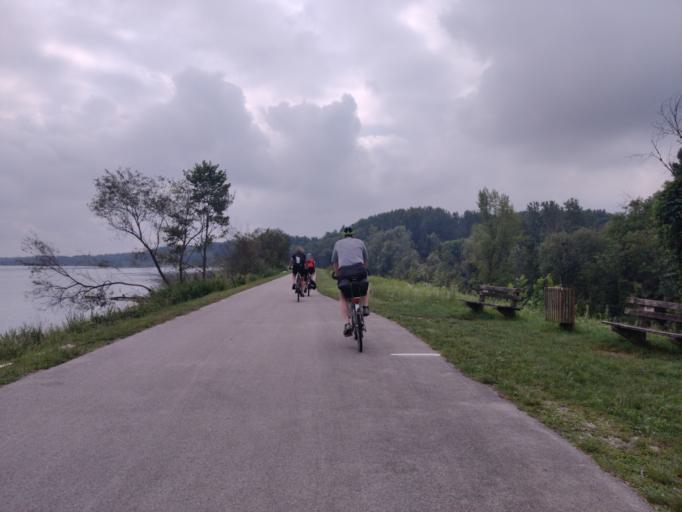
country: AT
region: Lower Austria
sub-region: Politischer Bezirk Sankt Polten
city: Traismauer
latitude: 48.3722
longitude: 15.7378
